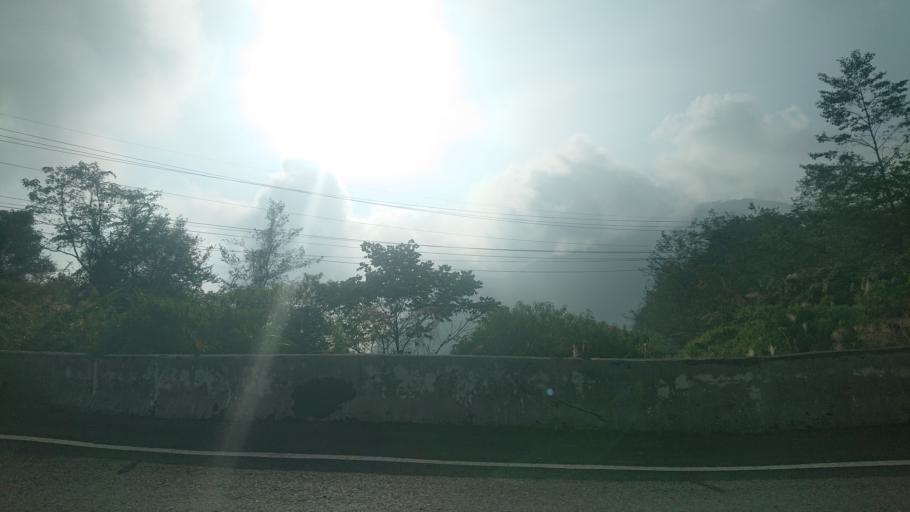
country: TW
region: Taiwan
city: Lugu
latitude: 23.4959
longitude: 120.7928
